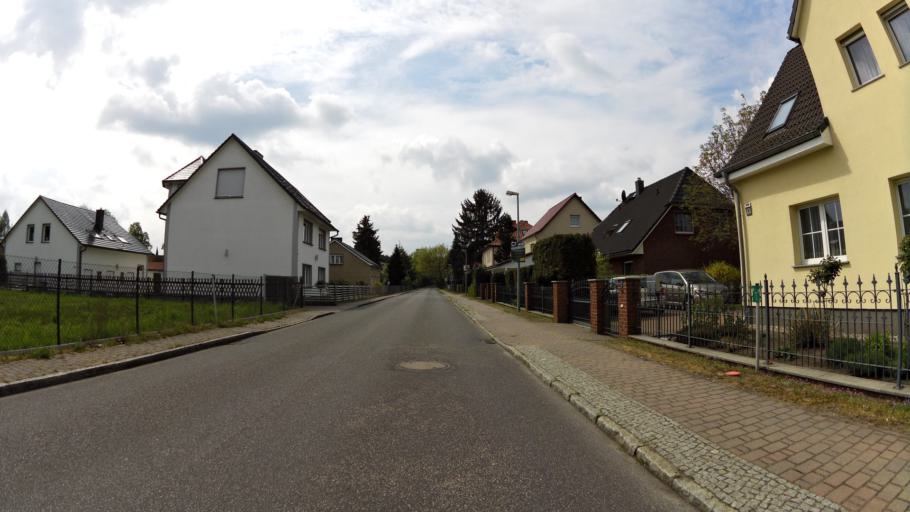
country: DE
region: Brandenburg
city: Bestensee
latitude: 52.2552
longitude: 13.7299
